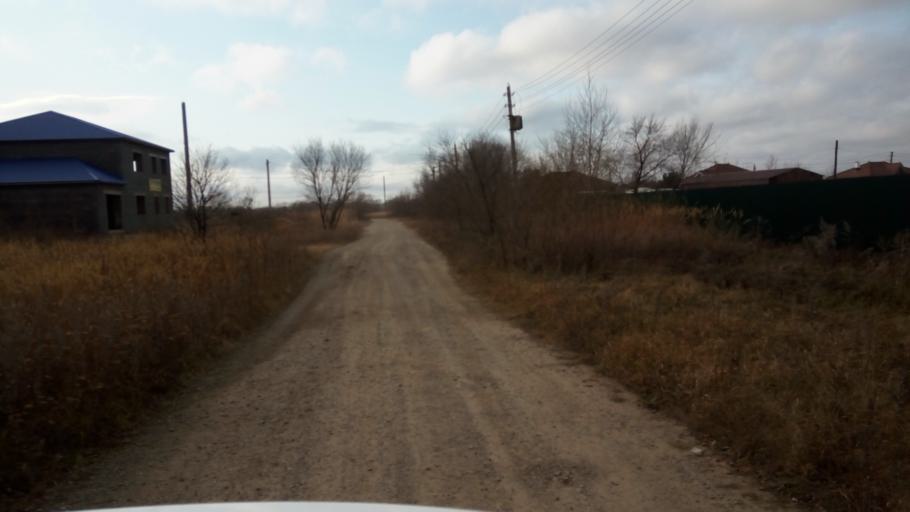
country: RU
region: Primorskiy
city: Ussuriysk
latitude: 43.7993
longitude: 131.9514
